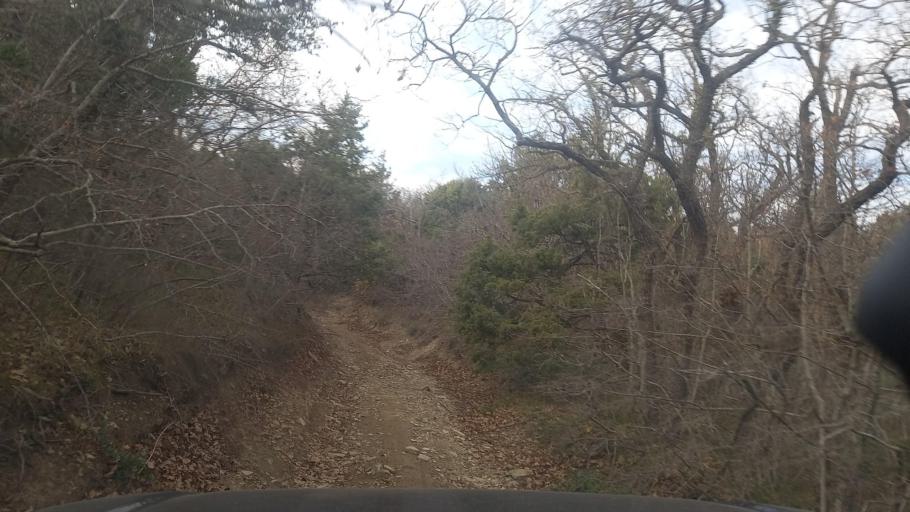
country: RU
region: Krasnodarskiy
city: Myskhako
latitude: 44.6671
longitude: 37.6740
